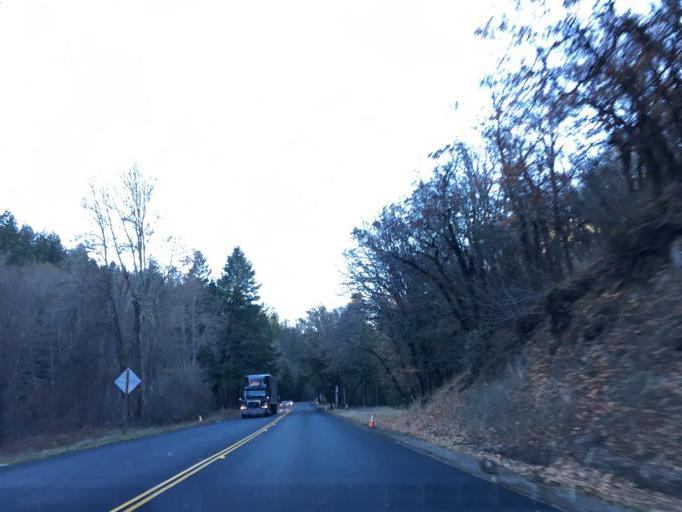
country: US
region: California
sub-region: Mendocino County
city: Laytonville
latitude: 39.8119
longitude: -123.5569
